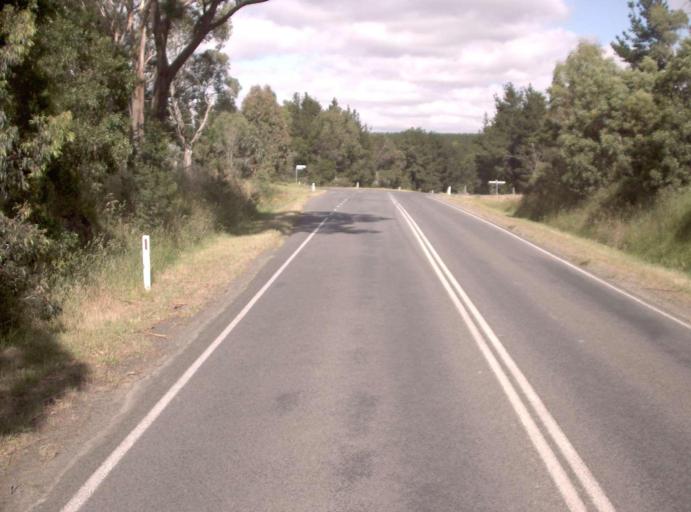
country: AU
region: Victoria
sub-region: Latrobe
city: Traralgon
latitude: -38.1890
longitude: 146.4882
